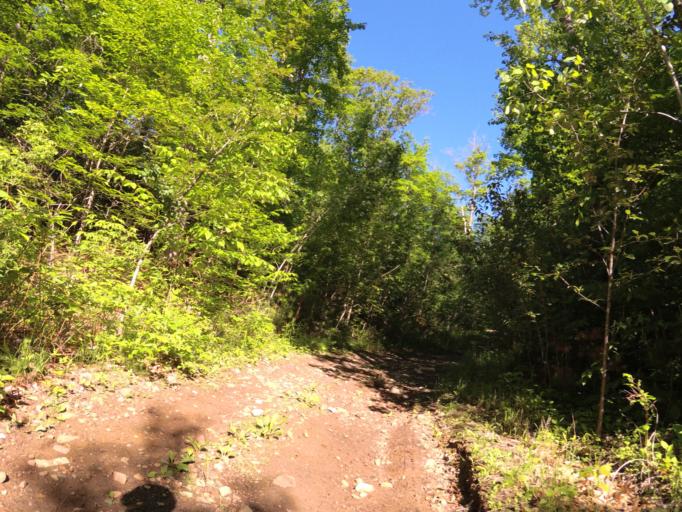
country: CA
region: Ontario
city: Renfrew
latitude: 45.1166
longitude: -77.0401
